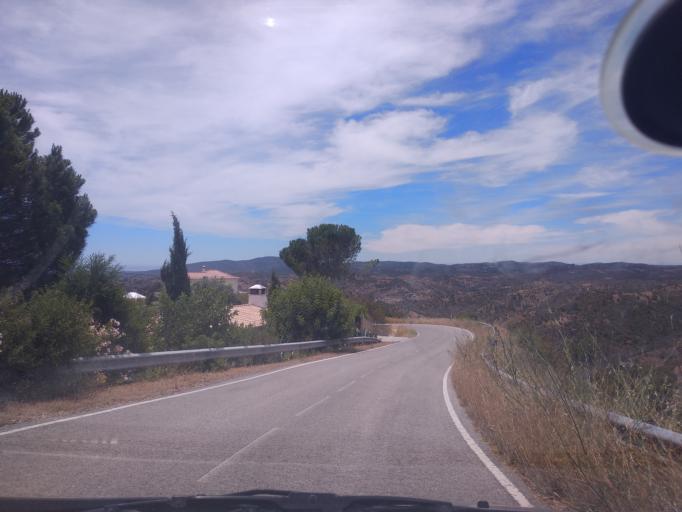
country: PT
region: Faro
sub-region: Sao Bras de Alportel
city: Sao Bras de Alportel
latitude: 37.1929
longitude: -7.7970
